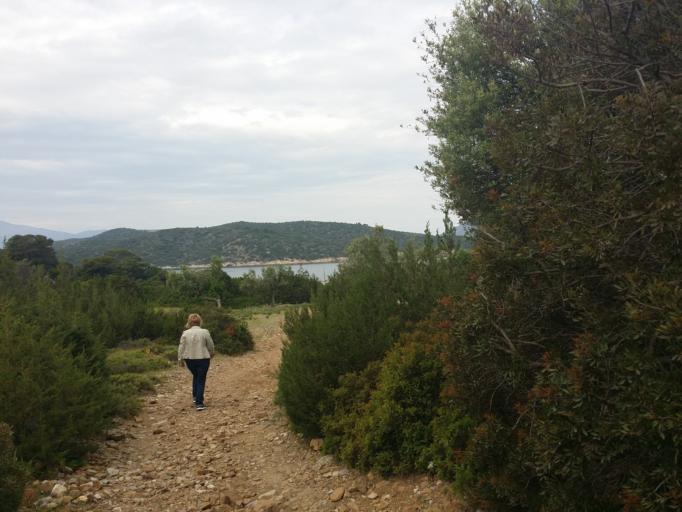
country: GR
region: Attica
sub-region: Nomos Piraios
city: Galatas
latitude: 37.5206
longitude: 23.4289
